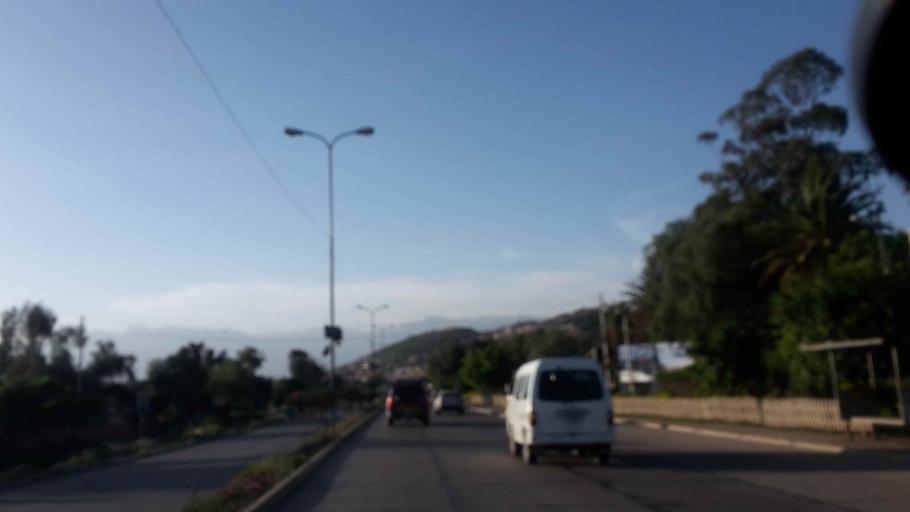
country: BO
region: Cochabamba
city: Cochabamba
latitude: -17.4543
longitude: -66.1268
